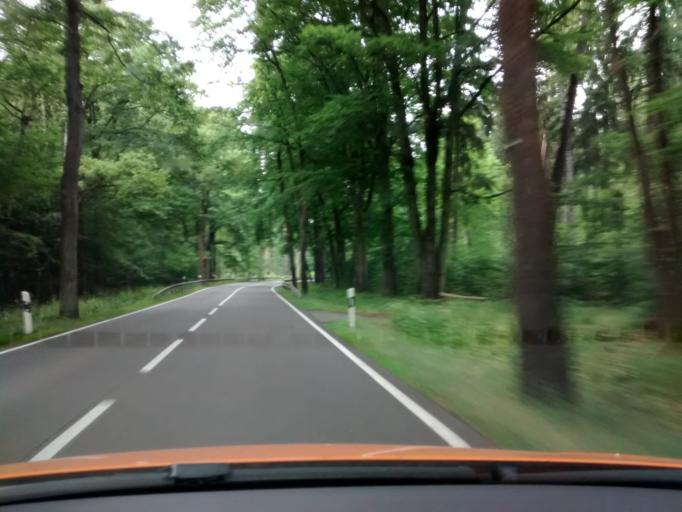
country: DE
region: Brandenburg
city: Wiesenburg
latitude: 52.0915
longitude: 12.4398
